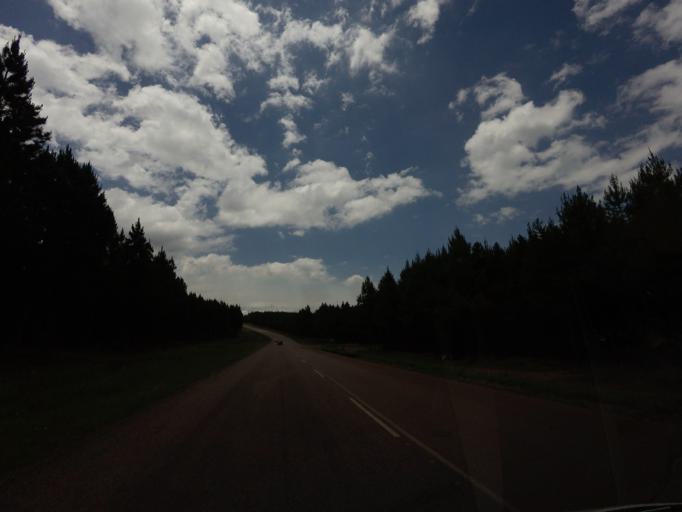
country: ZA
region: Mpumalanga
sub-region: Ehlanzeni District
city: Graksop
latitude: -25.0401
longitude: 30.8198
